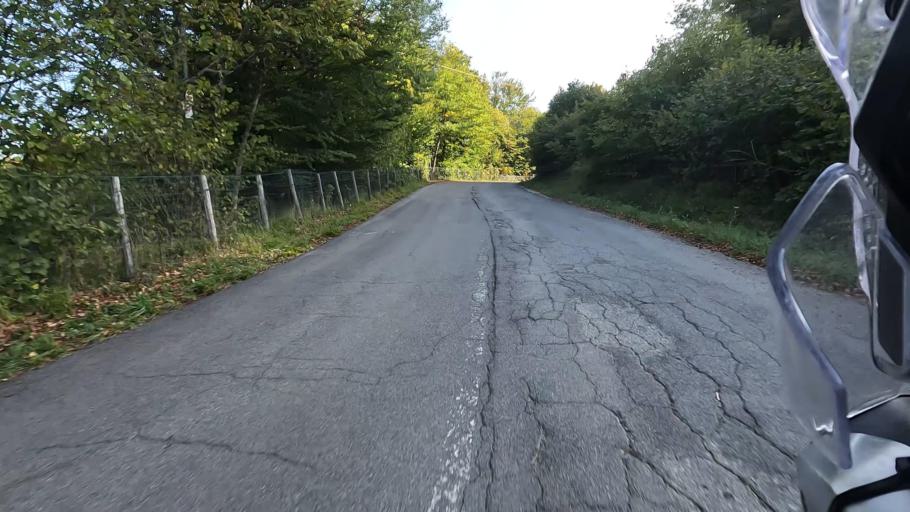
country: IT
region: Liguria
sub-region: Provincia di Savona
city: Urbe
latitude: 44.4714
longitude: 8.5613
